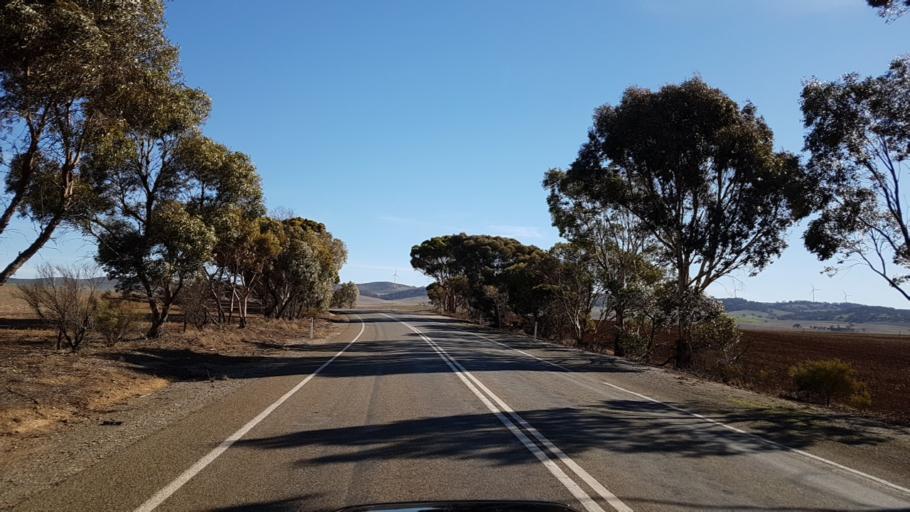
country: AU
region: South Australia
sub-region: Northern Areas
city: Jamestown
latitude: -33.0408
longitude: 138.6300
